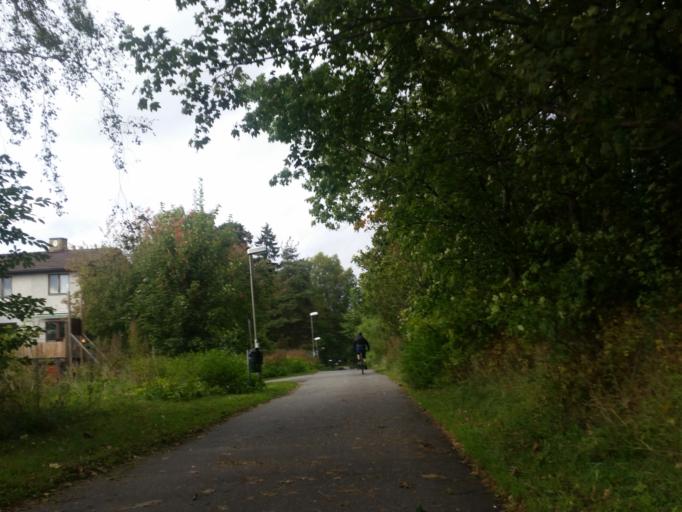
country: SE
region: Stockholm
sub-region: Stockholms Kommun
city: Arsta
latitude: 59.2640
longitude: 18.0978
